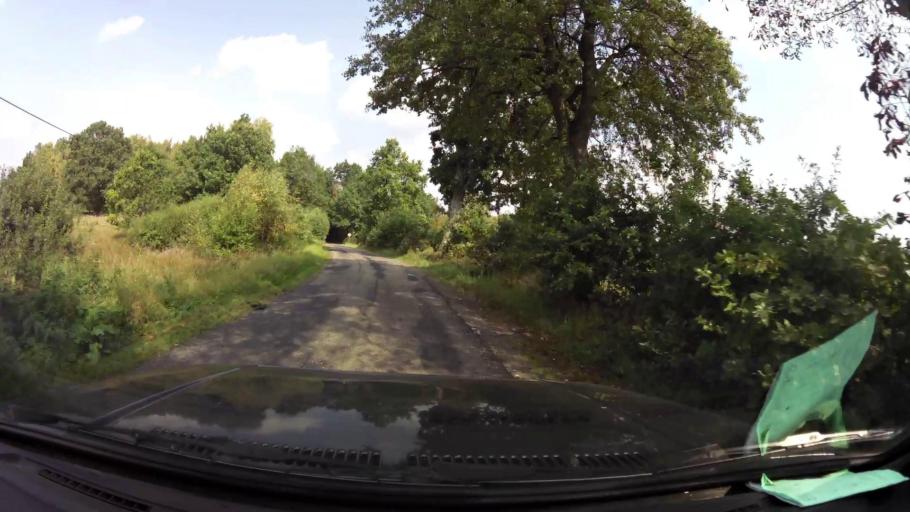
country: PL
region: West Pomeranian Voivodeship
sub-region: Powiat koszalinski
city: Polanow
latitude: 54.1262
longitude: 16.5184
